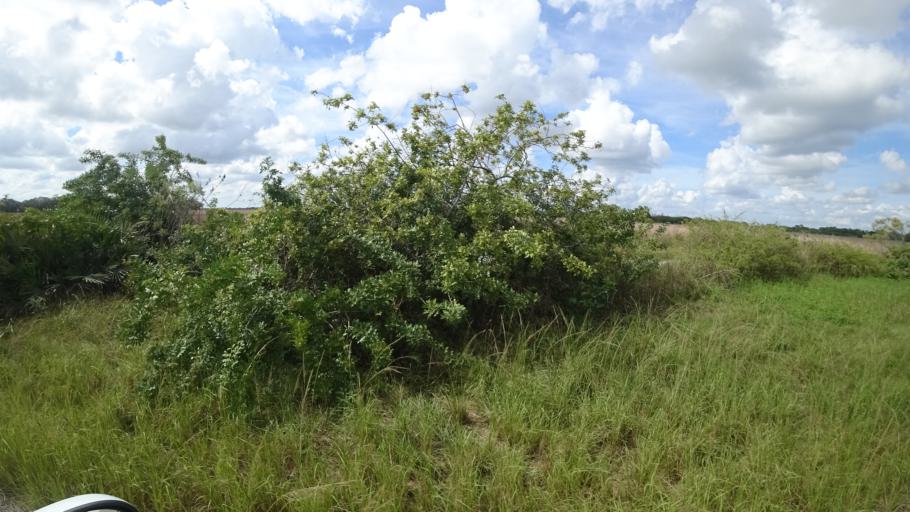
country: US
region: Florida
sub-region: Hillsborough County
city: Wimauma
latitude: 27.5902
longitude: -82.2663
